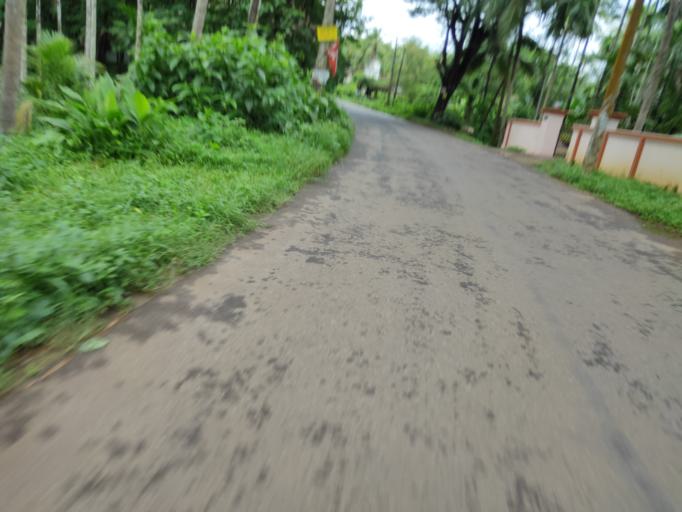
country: IN
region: Kerala
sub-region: Malappuram
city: Manjeri
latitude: 11.1853
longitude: 76.2061
